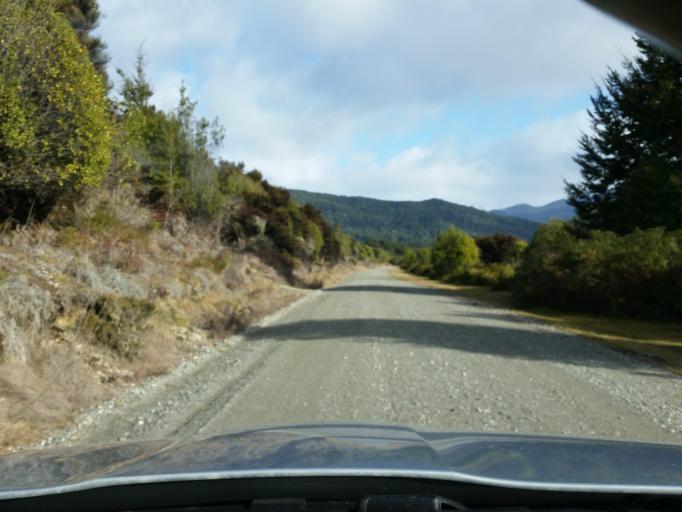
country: NZ
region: Southland
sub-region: Southland District
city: Te Anau
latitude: -45.5583
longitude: 167.6190
